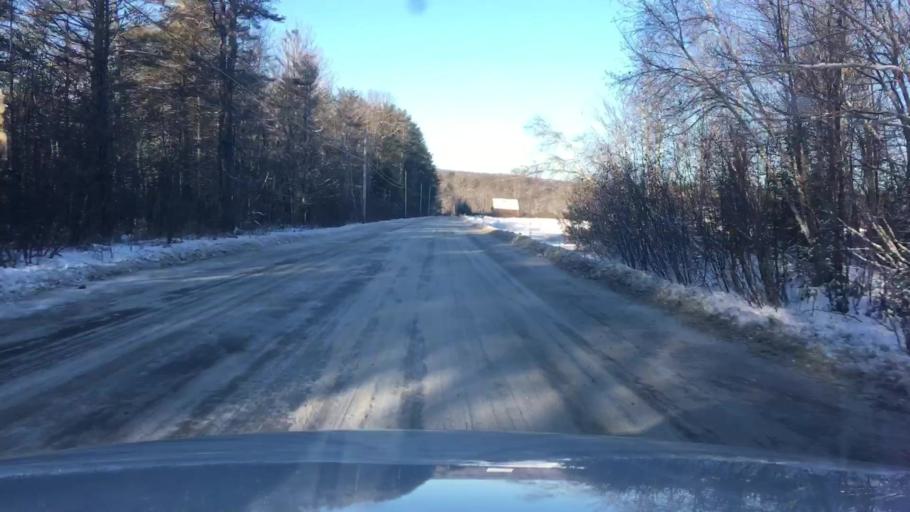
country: US
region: Maine
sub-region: Kennebec County
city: Belgrade
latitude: 44.4280
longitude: -69.8964
